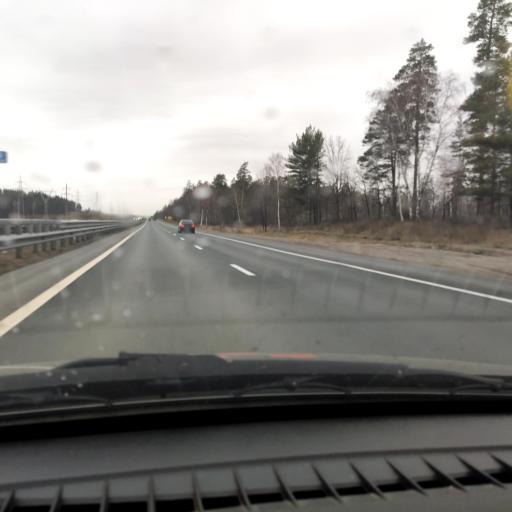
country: RU
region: Samara
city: Povolzhskiy
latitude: 53.5167
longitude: 49.7264
